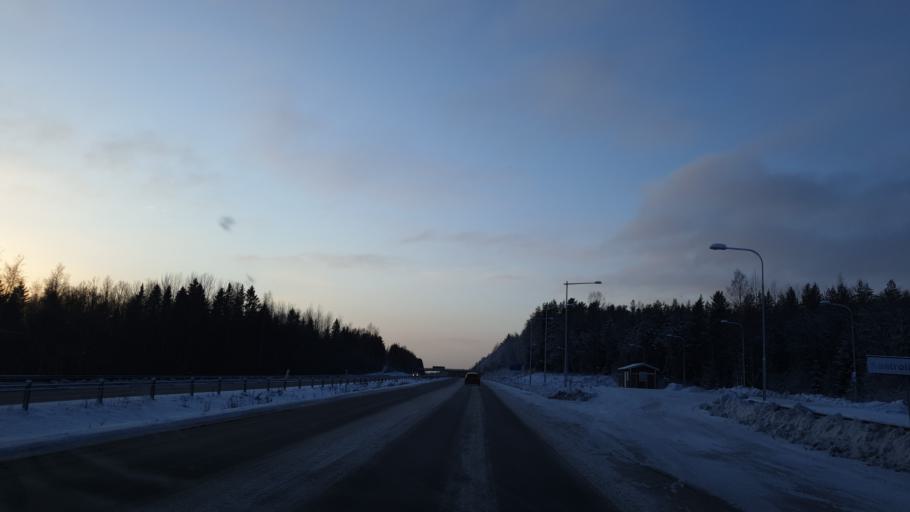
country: SE
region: Vaesterbotten
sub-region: Umea Kommun
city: Roback
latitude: 63.7957
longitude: 20.2217
